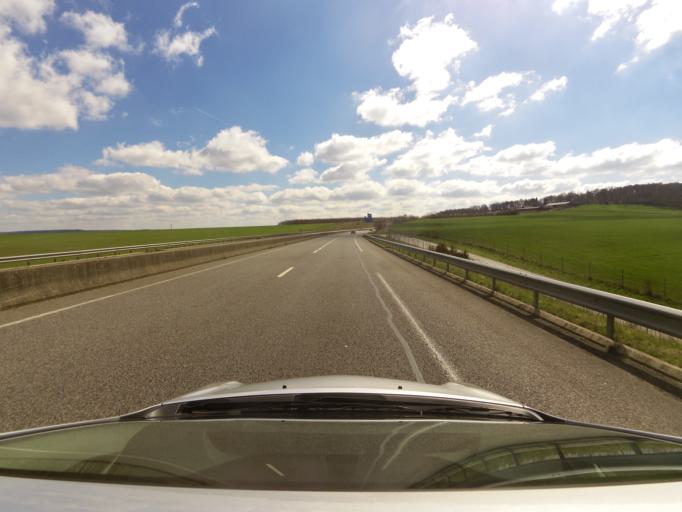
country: FR
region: Haute-Normandie
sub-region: Departement de la Seine-Maritime
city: Neufchatel-en-Bray
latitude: 49.7647
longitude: 1.4800
